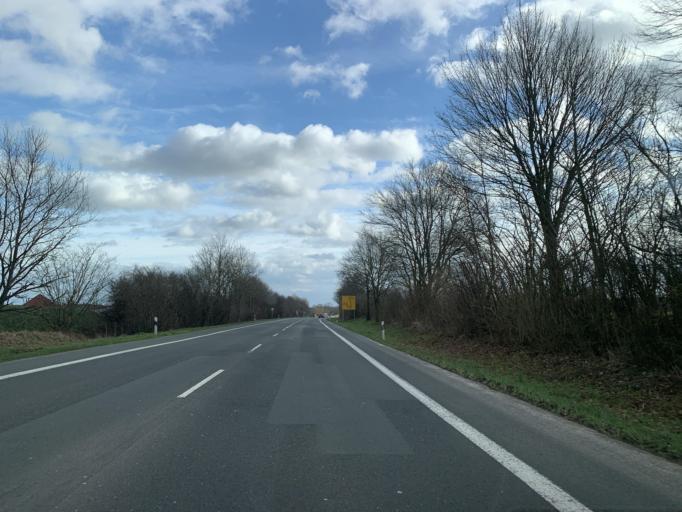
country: DE
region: North Rhine-Westphalia
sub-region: Regierungsbezirk Munster
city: Horstmar
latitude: 52.0730
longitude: 7.3080
